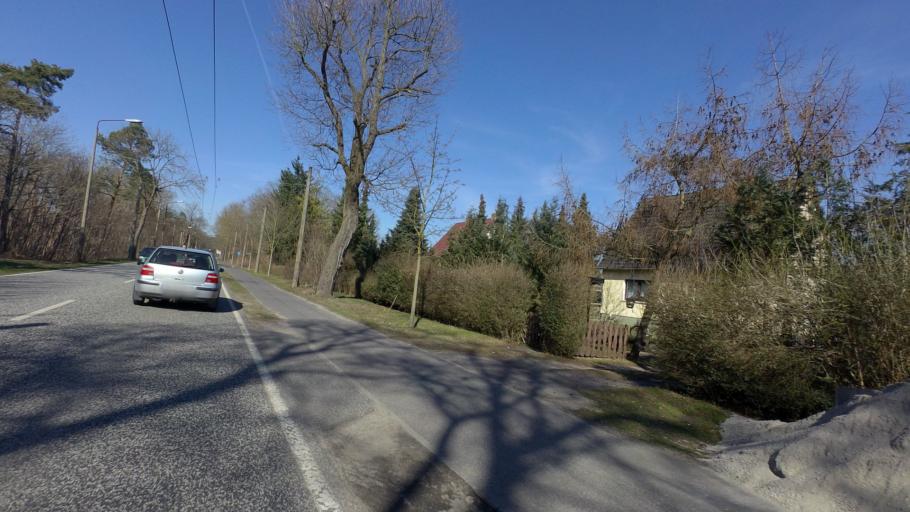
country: DE
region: Brandenburg
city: Eberswalde
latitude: 52.8485
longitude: 13.8243
